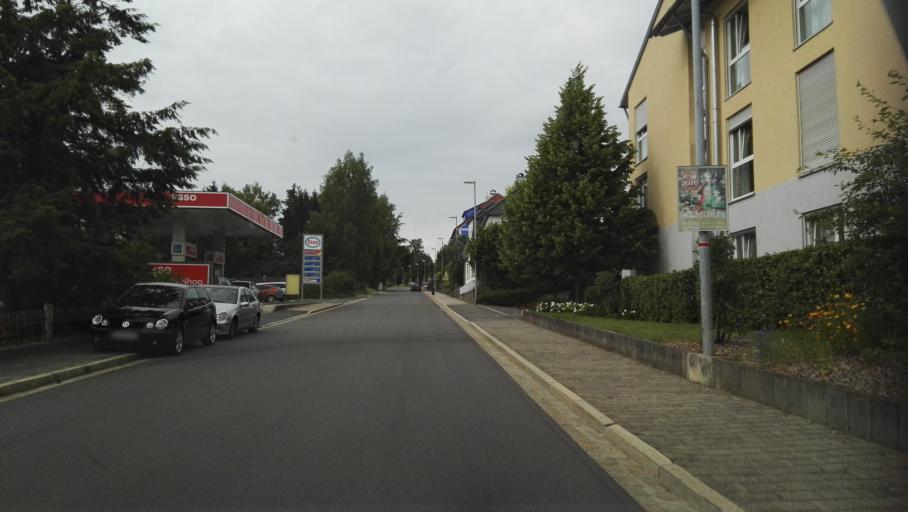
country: DE
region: Bavaria
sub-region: Upper Franconia
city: Hollfeld
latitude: 49.9392
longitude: 11.2885
